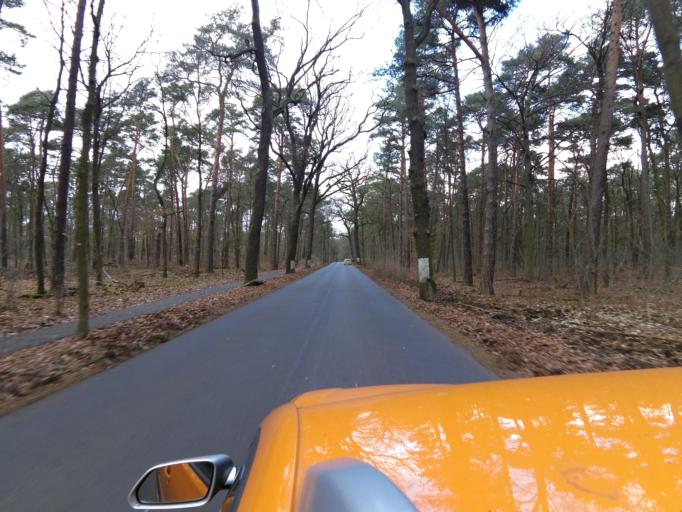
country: DE
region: Berlin
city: Nikolassee
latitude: 52.4458
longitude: 13.1977
